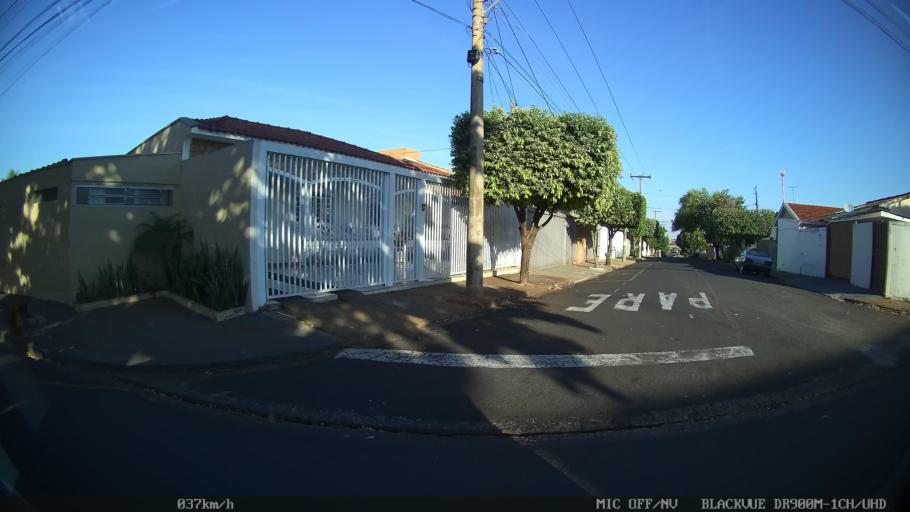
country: BR
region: Sao Paulo
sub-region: Sao Jose Do Rio Preto
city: Sao Jose do Rio Preto
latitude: -20.7988
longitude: -49.3634
